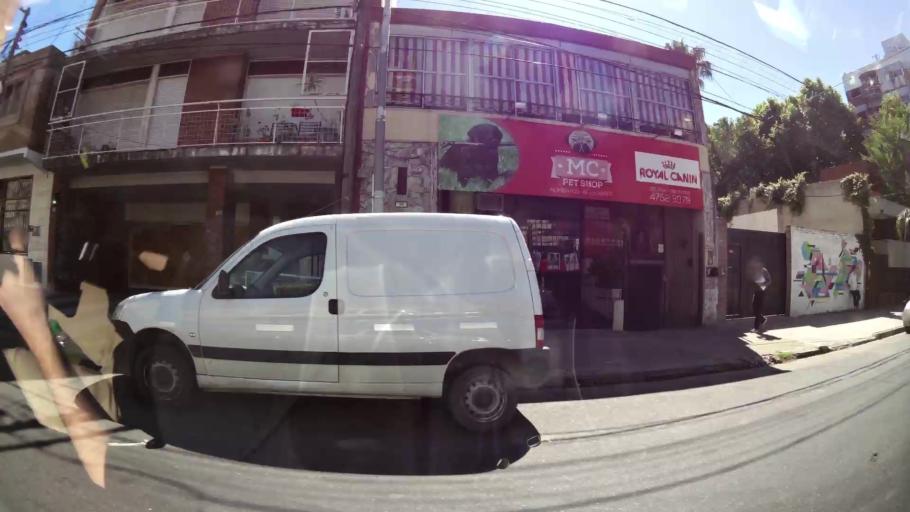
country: AR
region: Buenos Aires
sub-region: Partido de General San Martin
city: General San Martin
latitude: -34.5795
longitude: -58.5339
